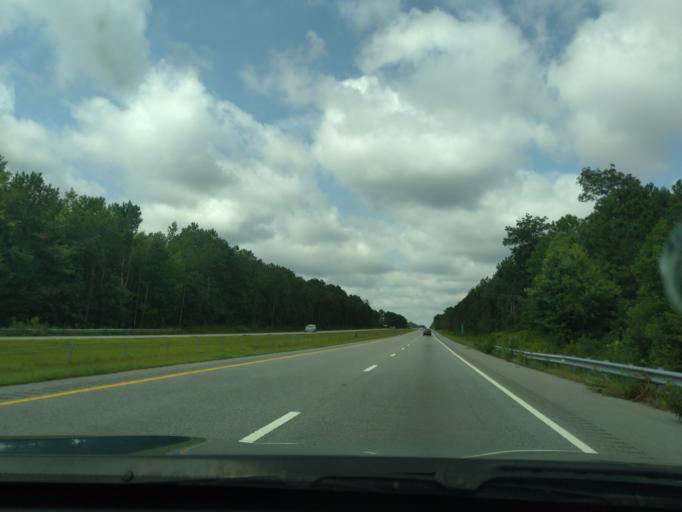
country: US
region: North Carolina
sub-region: Martin County
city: Williamston
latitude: 35.8280
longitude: -77.1367
